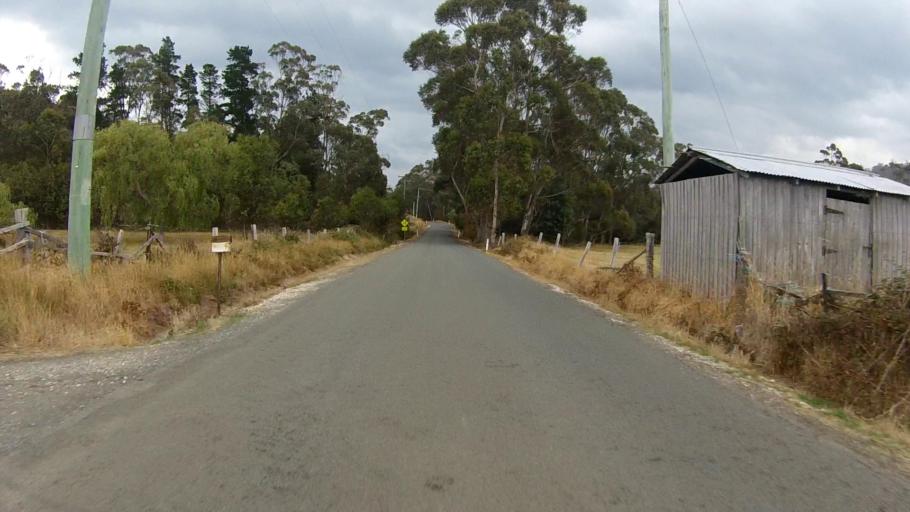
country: AU
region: Tasmania
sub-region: Huon Valley
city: Cygnet
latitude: -43.2392
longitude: 147.1534
